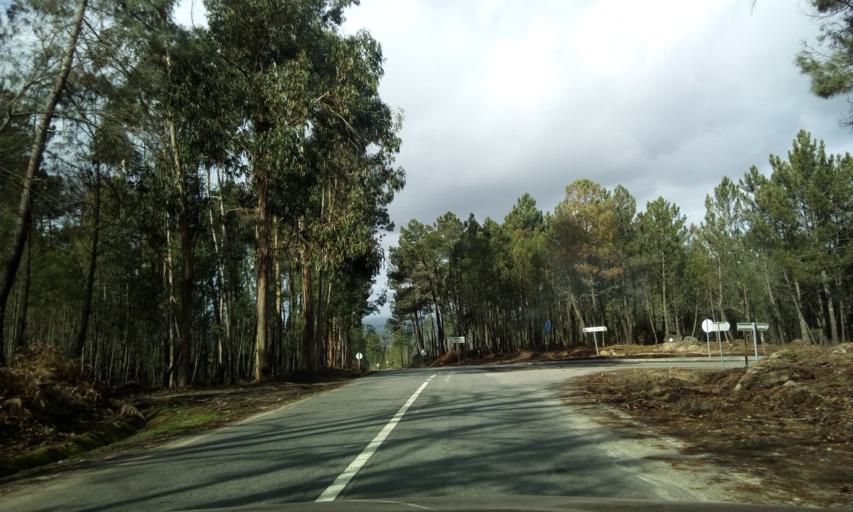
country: PT
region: Guarda
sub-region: Fornos de Algodres
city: Fornos de Algodres
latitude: 40.6620
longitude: -7.6419
